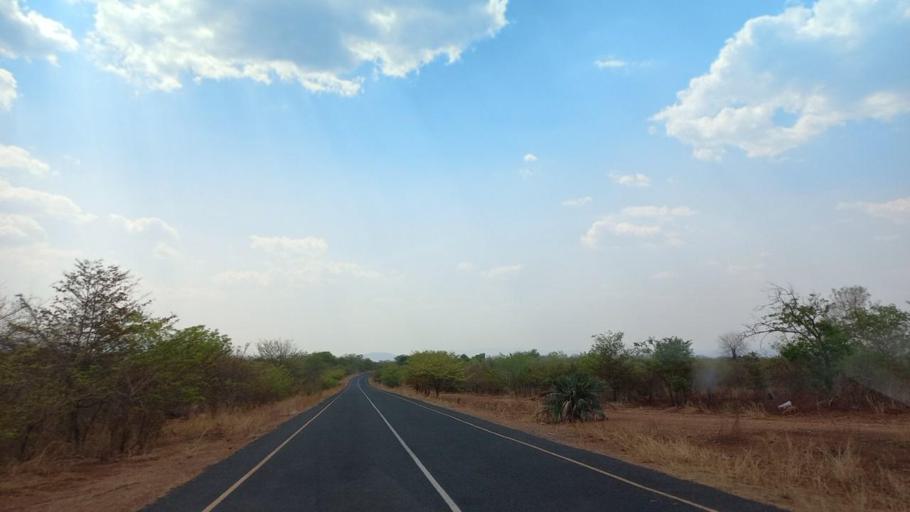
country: ZM
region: Lusaka
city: Luangwa
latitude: -15.2157
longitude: 30.2326
